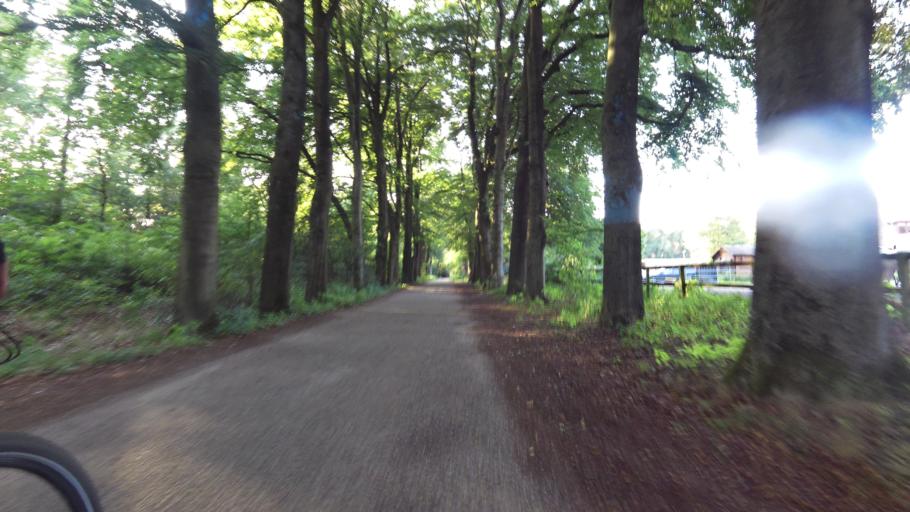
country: NL
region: Gelderland
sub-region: Gemeente Renkum
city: Oosterbeek
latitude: 52.0215
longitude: 5.8399
